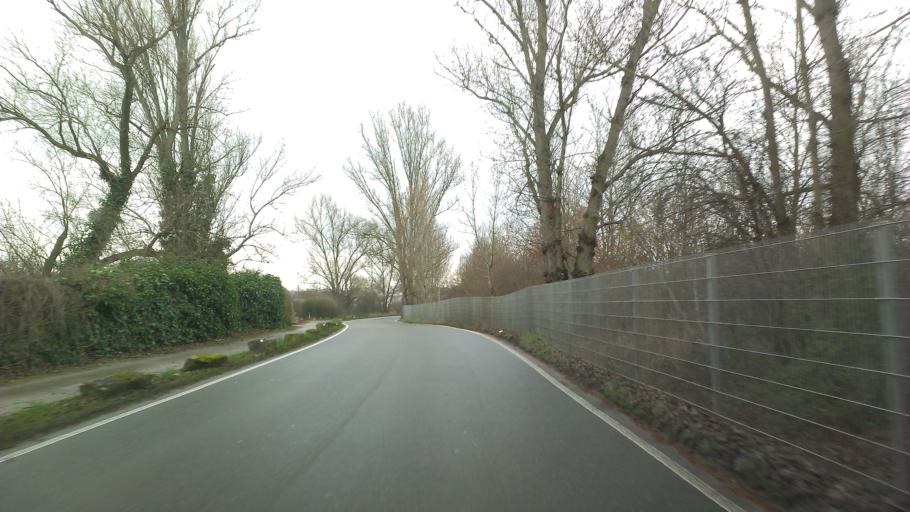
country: DE
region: Rheinland-Pfalz
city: Gartenstadt
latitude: 49.4982
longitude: 8.3833
